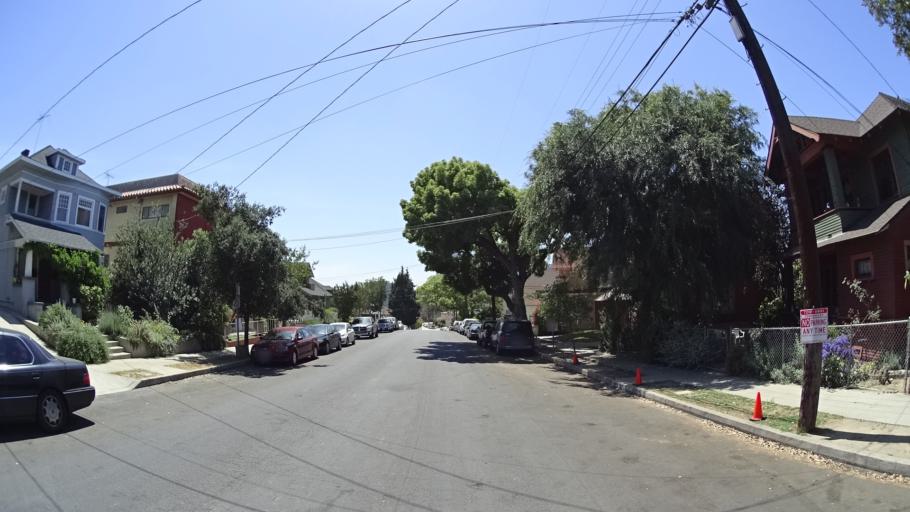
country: US
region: California
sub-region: Los Angeles County
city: Echo Park
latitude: 34.0693
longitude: -118.2517
